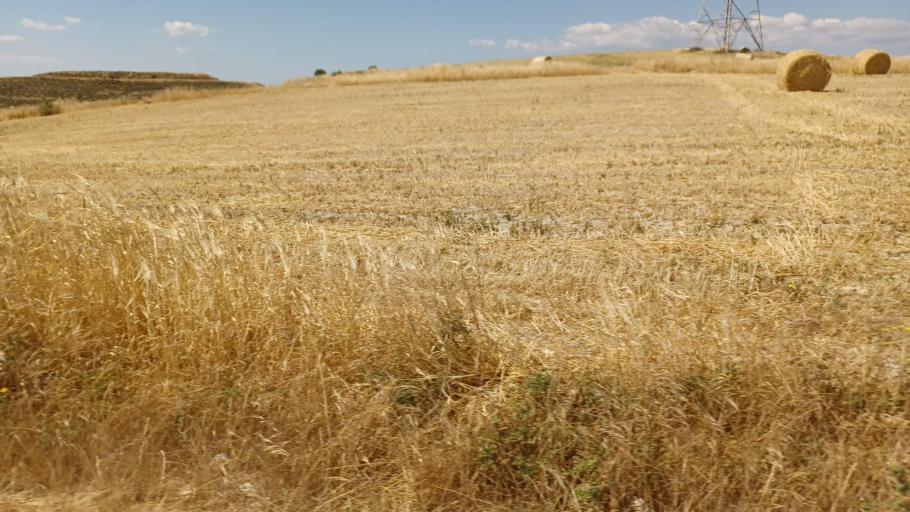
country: CY
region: Larnaka
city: Aradippou
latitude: 34.9941
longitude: 33.5478
